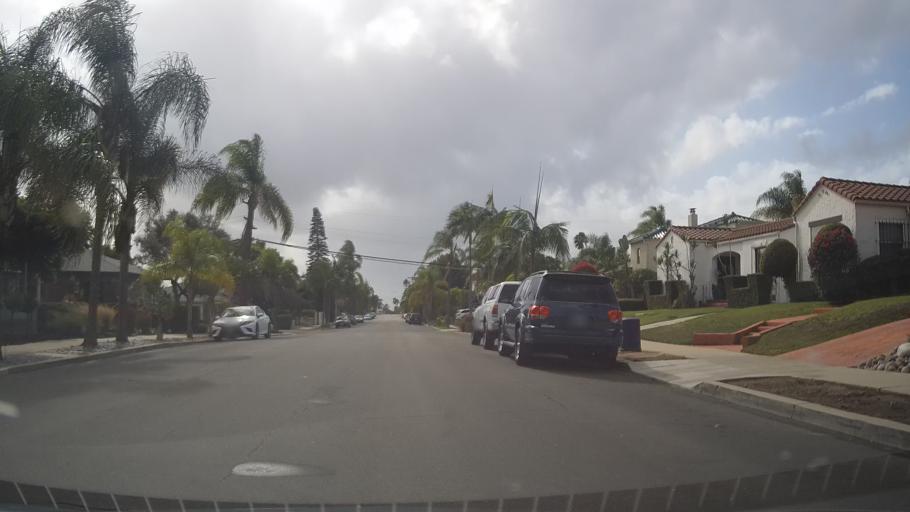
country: US
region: California
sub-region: San Diego County
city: San Diego
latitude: 32.7325
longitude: -117.1244
